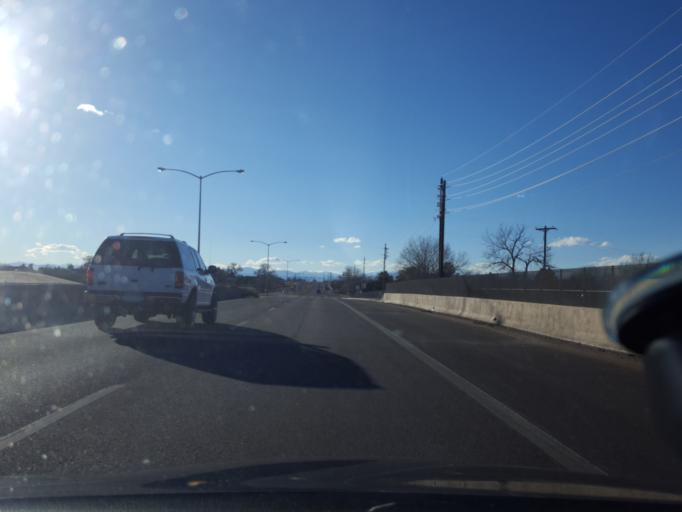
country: US
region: Colorado
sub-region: Adams County
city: Aurora
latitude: 39.7403
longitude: -104.7803
